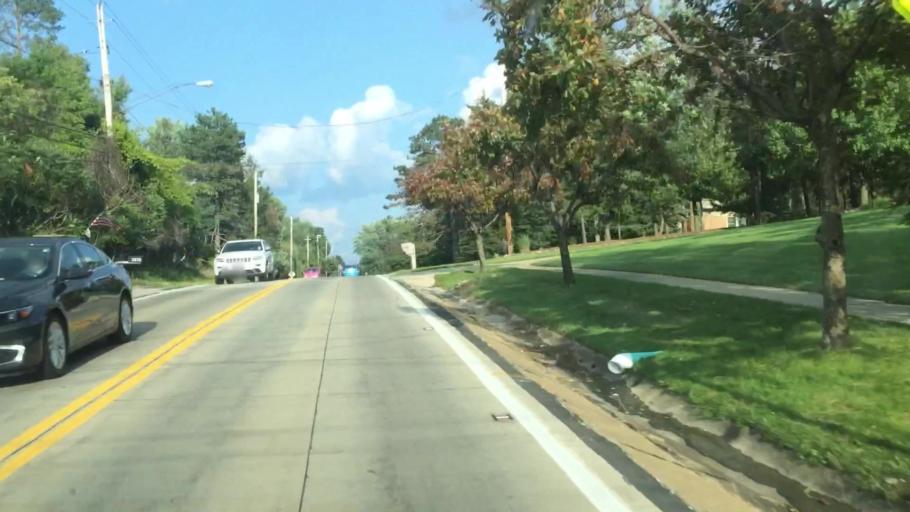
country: US
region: Ohio
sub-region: Cuyahoga County
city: North Royalton
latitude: 41.3510
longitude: -81.7103
